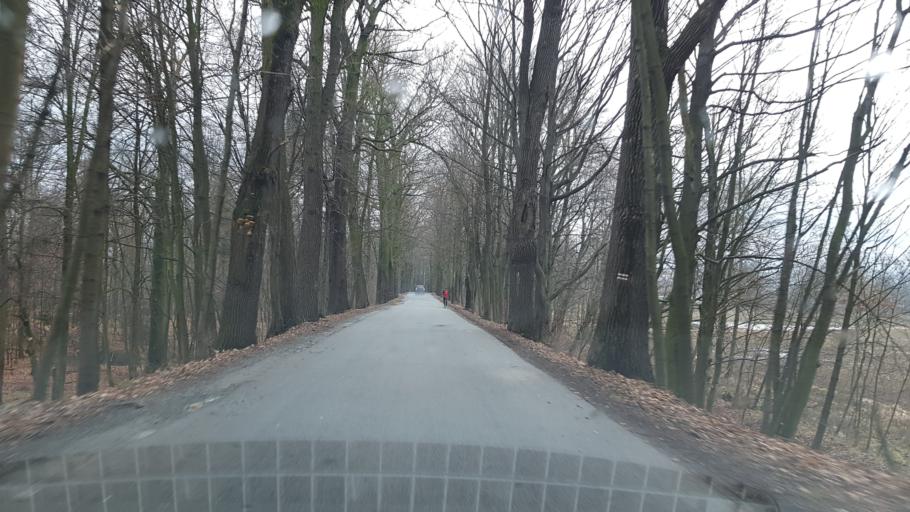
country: PL
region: Silesian Voivodeship
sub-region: Powiat pszczynski
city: Radostowice
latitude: 49.9724
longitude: 18.9060
